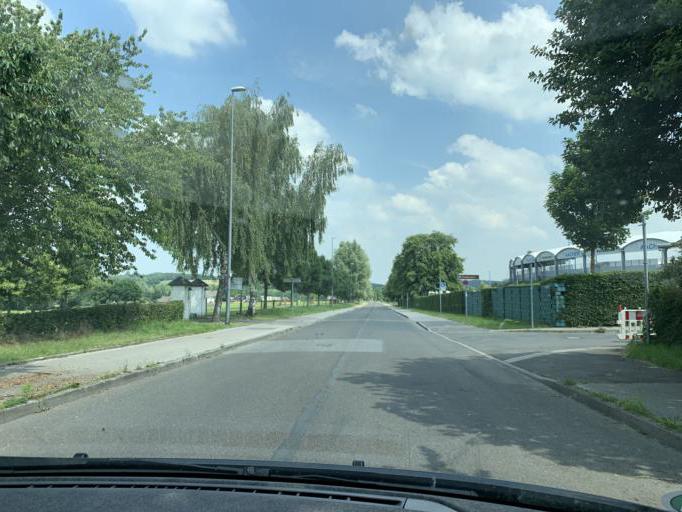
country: DE
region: North Rhine-Westphalia
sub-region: Regierungsbezirk Koln
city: Aachen
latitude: 50.7951
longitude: 6.0917
